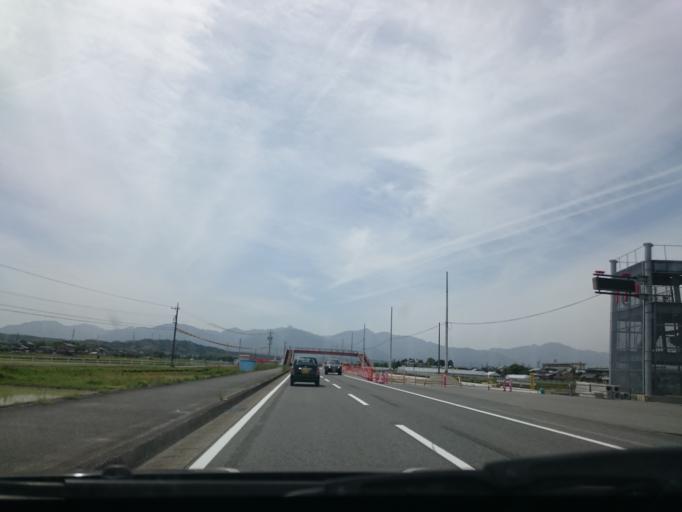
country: JP
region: Mie
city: Yokkaichi
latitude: 34.9819
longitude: 136.5719
